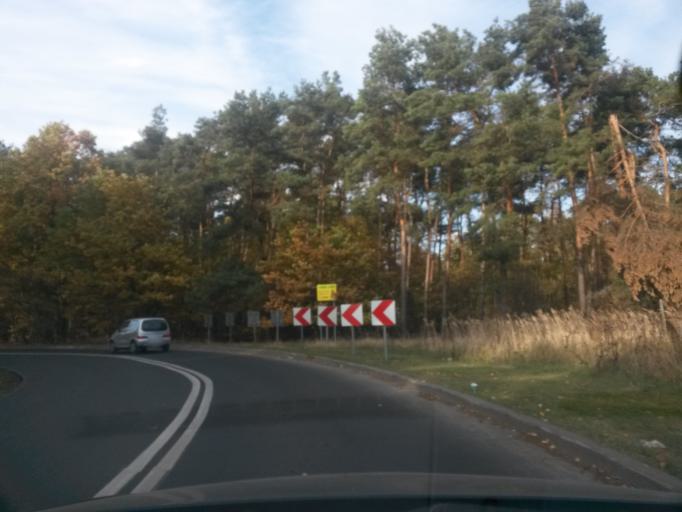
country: PL
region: Greater Poland Voivodeship
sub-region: Powiat poznanski
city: Plewiska
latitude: 52.3921
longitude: 16.8268
